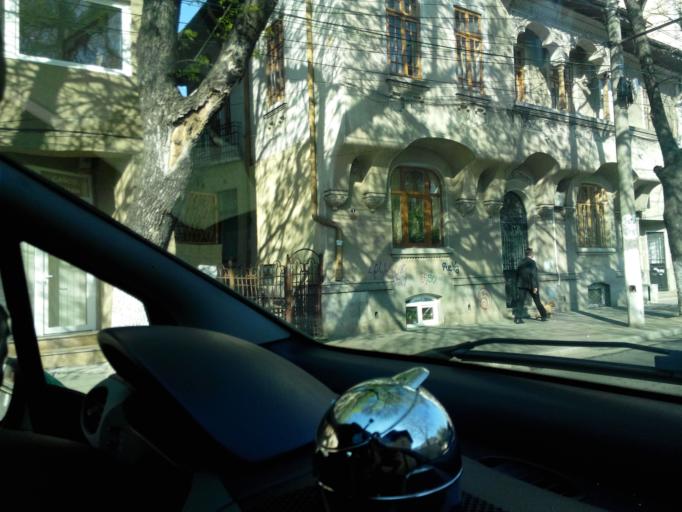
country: RO
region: Bucuresti
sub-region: Municipiul Bucuresti
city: Bucharest
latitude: 44.4386
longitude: 26.1231
